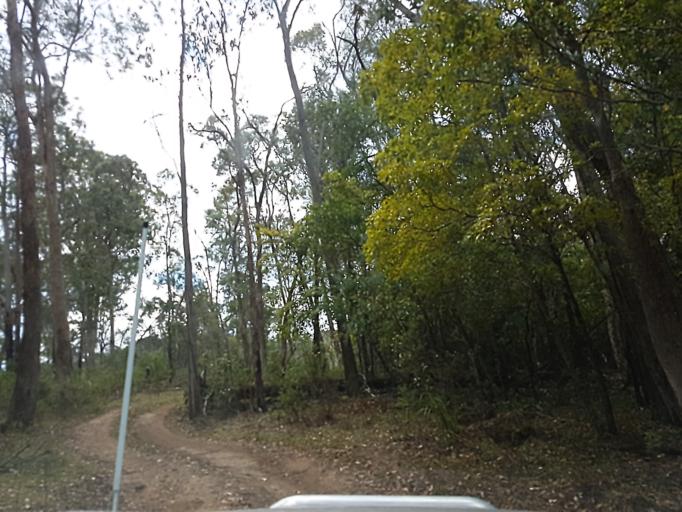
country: AU
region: Victoria
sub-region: East Gippsland
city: Lakes Entrance
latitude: -37.3637
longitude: 148.3520
